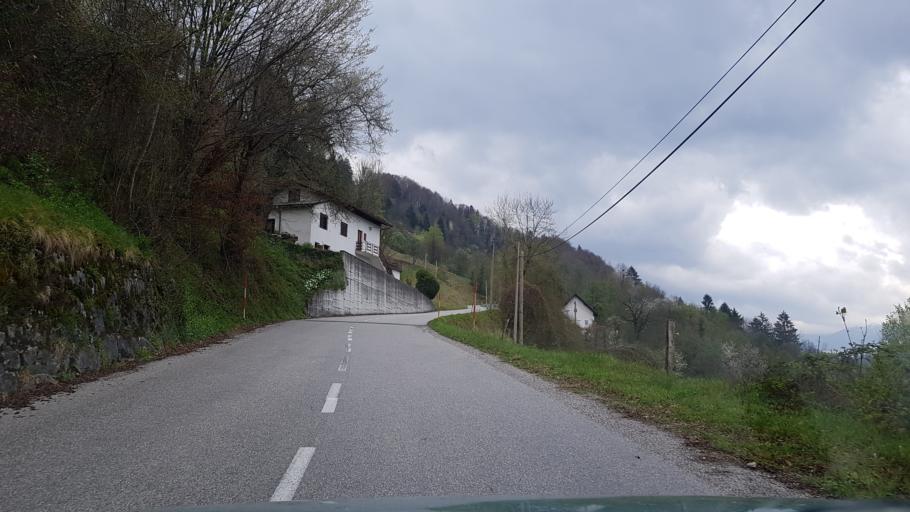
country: SI
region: Tolmin
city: Tolmin
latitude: 46.1181
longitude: 13.8169
